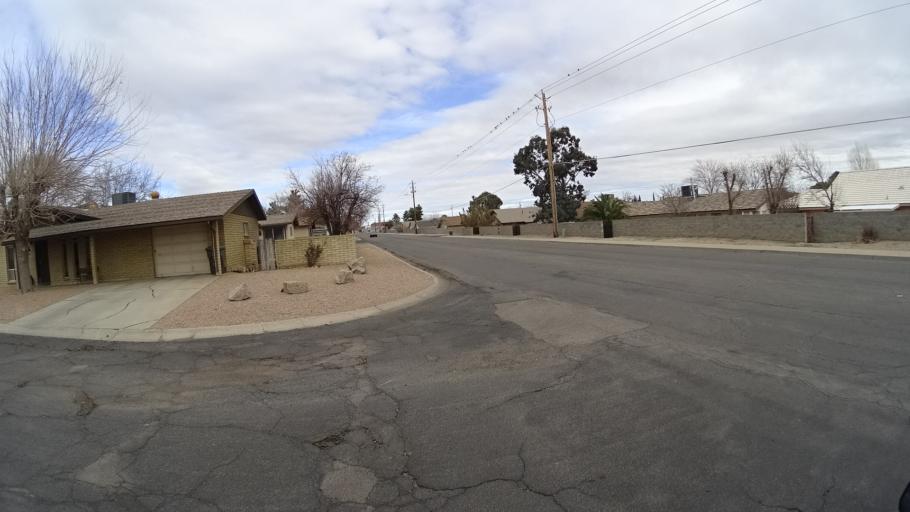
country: US
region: Arizona
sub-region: Mohave County
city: New Kingman-Butler
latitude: 35.2371
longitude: -114.0404
